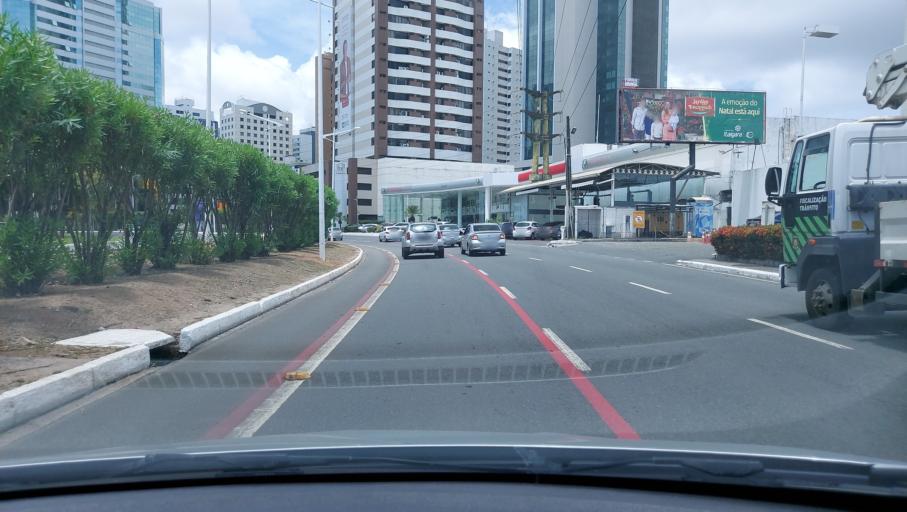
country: BR
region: Bahia
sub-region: Salvador
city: Salvador
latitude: -12.9888
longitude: -38.4497
